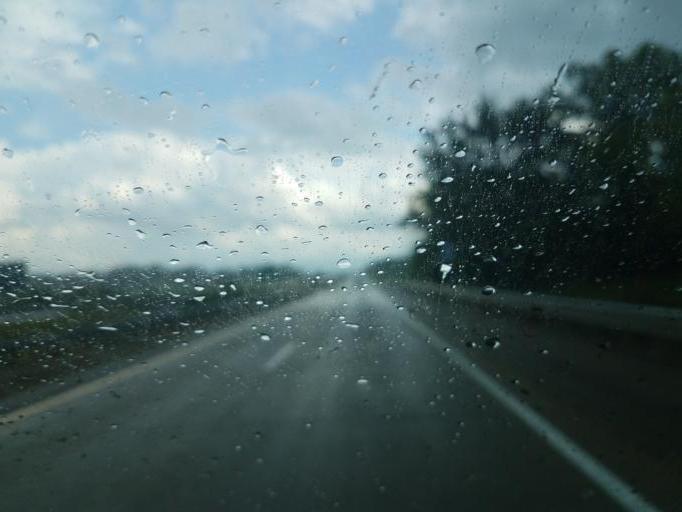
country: US
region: Michigan
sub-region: Calhoun County
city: Marshall
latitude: 42.2630
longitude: -84.9888
